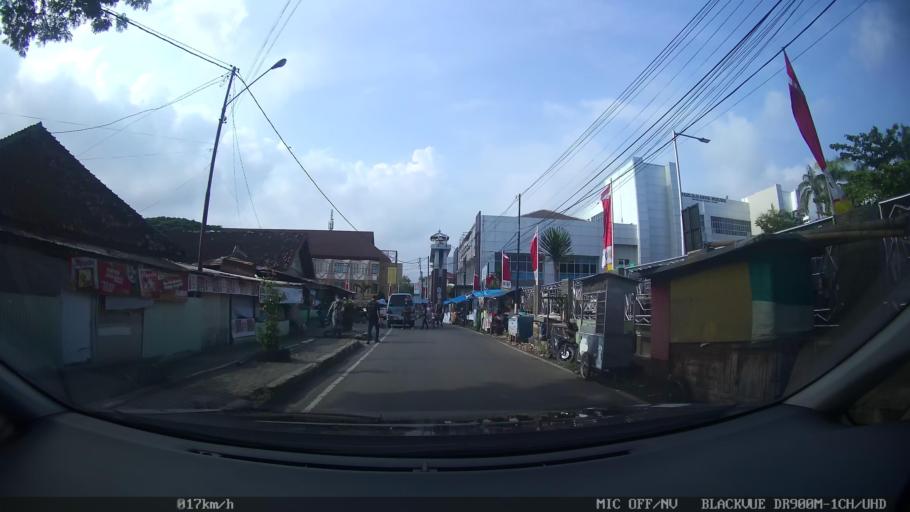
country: ID
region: Lampung
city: Kedaton
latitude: -5.4023
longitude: 105.2588
